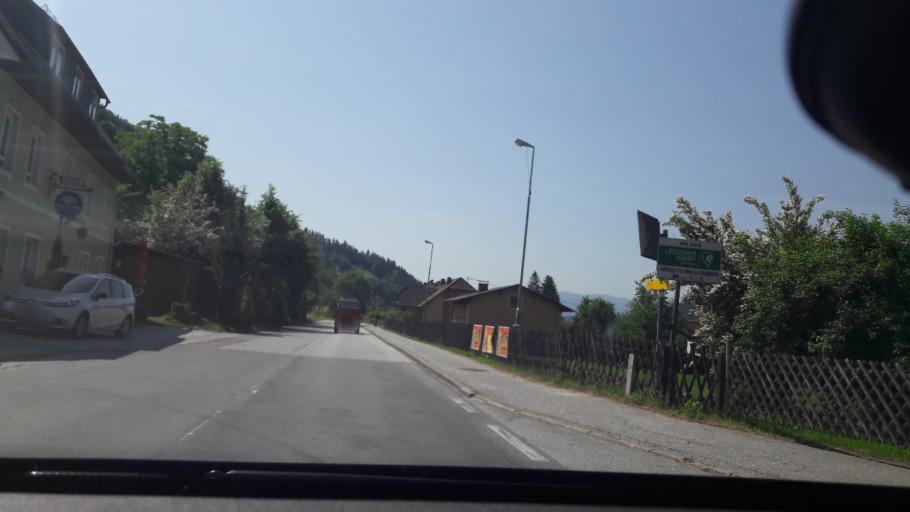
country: AT
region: Styria
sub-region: Politischer Bezirk Voitsberg
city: Kohlschwarz
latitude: 47.1073
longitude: 15.1205
